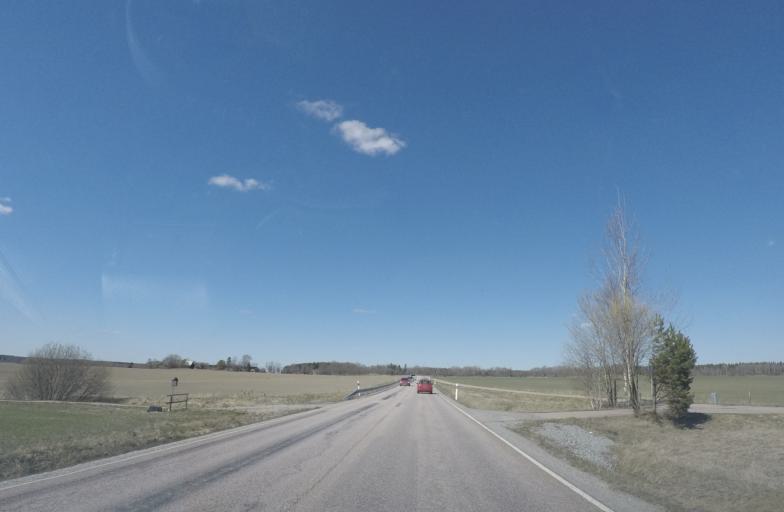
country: SE
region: Vaestmanland
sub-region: Vasteras
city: Vasteras
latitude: 59.6557
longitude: 16.4922
